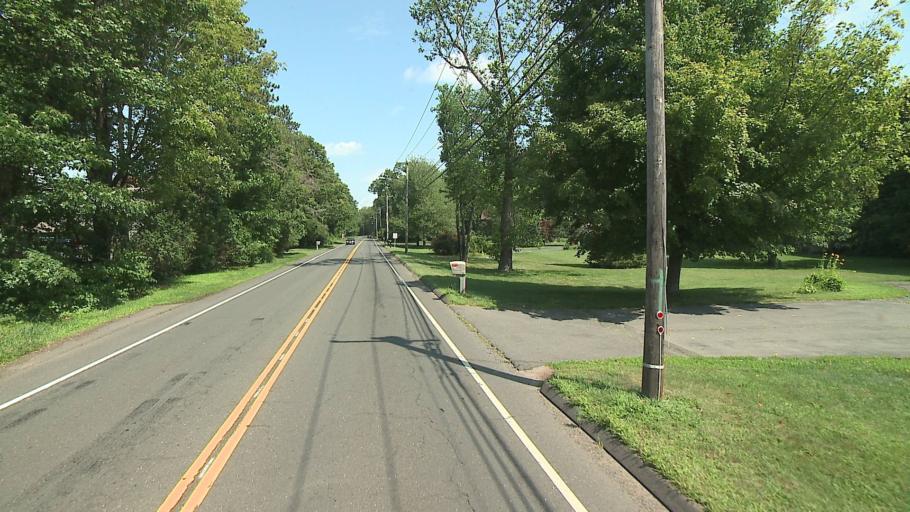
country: US
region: Connecticut
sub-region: Hartford County
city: Plainville
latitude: 41.7146
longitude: -72.8818
